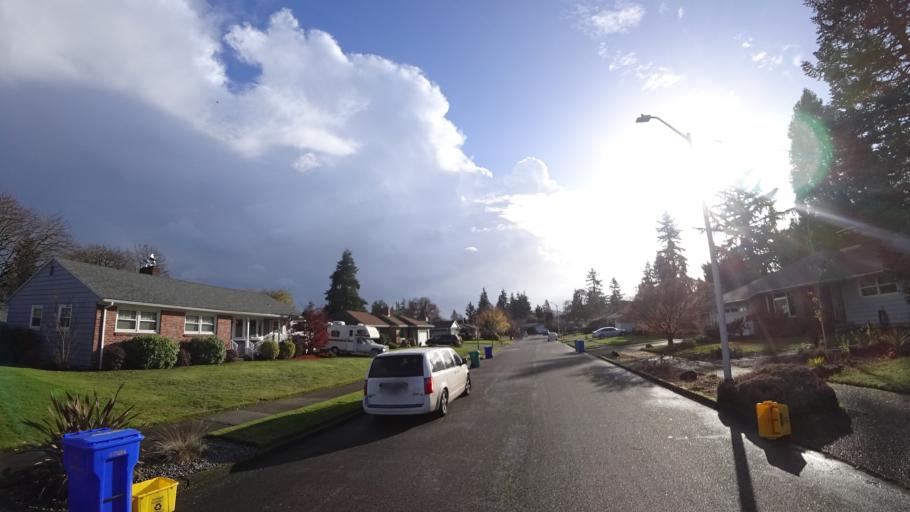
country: US
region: Oregon
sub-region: Multnomah County
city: Lents
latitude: 45.5250
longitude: -122.5551
